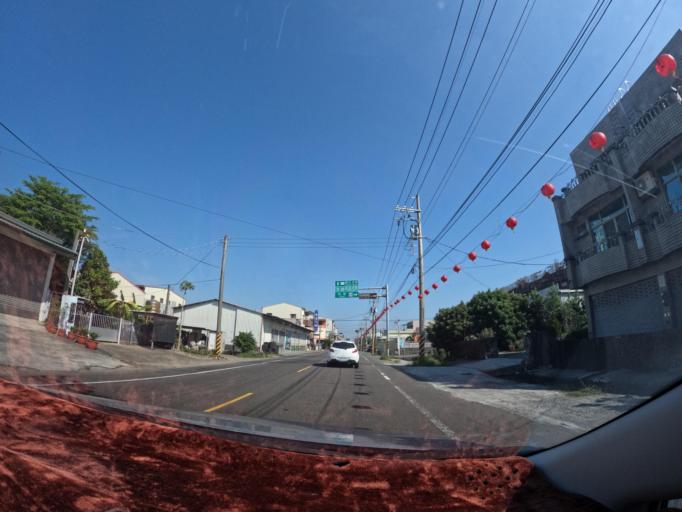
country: TW
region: Taiwan
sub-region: Tainan
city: Tainan
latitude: 23.0272
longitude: 120.2927
